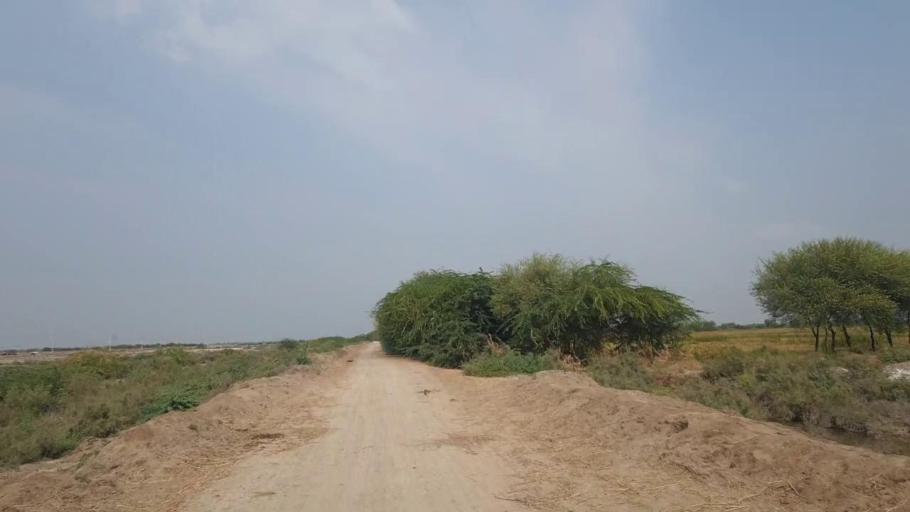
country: PK
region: Sindh
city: Badin
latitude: 24.5564
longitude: 68.7317
